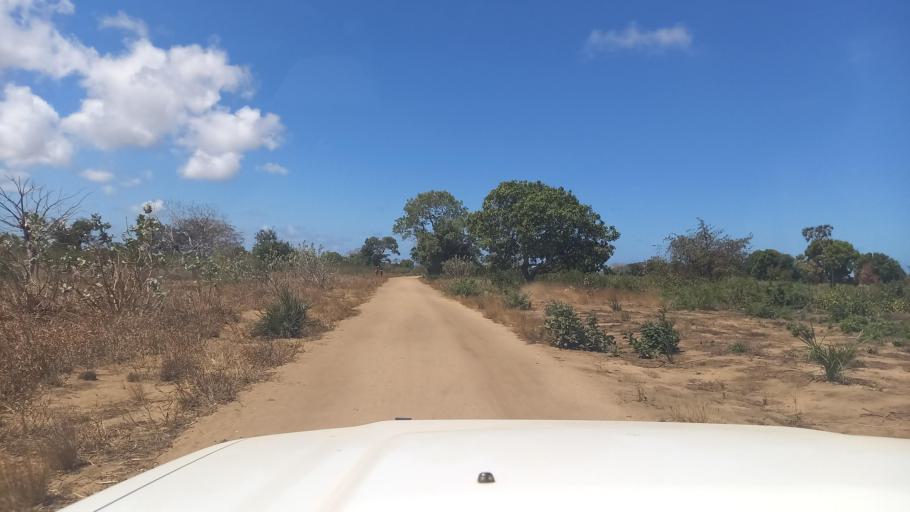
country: MZ
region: Cabo Delgado
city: Pemba
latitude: -13.4225
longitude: 40.5055
